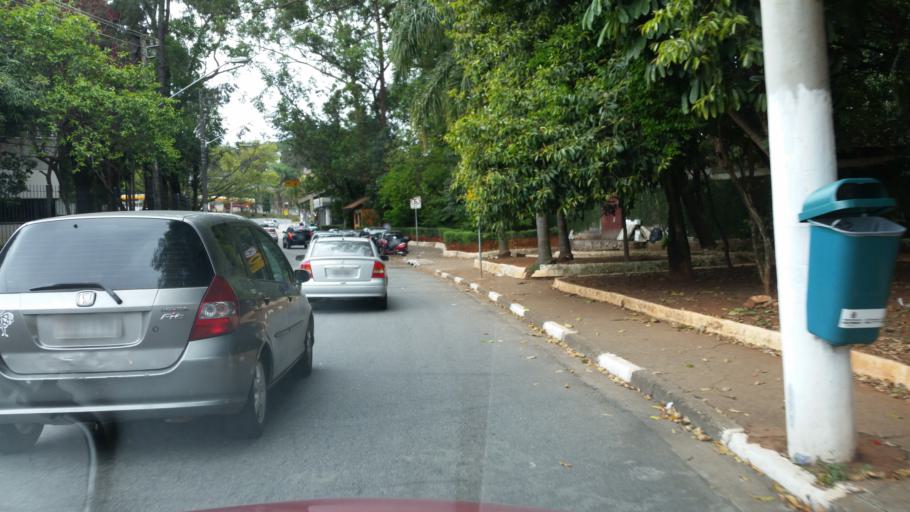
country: BR
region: Sao Paulo
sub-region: Diadema
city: Diadema
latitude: -23.6617
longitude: -46.6867
